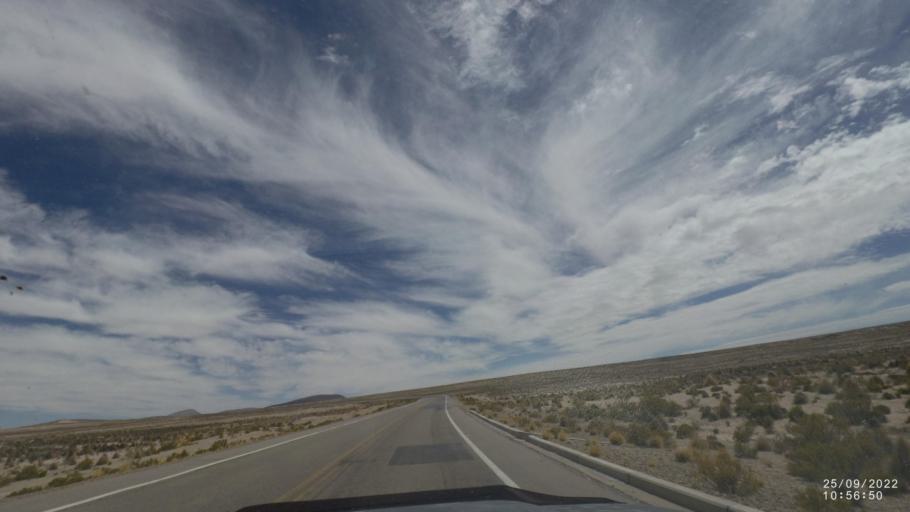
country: BO
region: Oruro
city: Challapata
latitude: -19.4797
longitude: -66.8824
